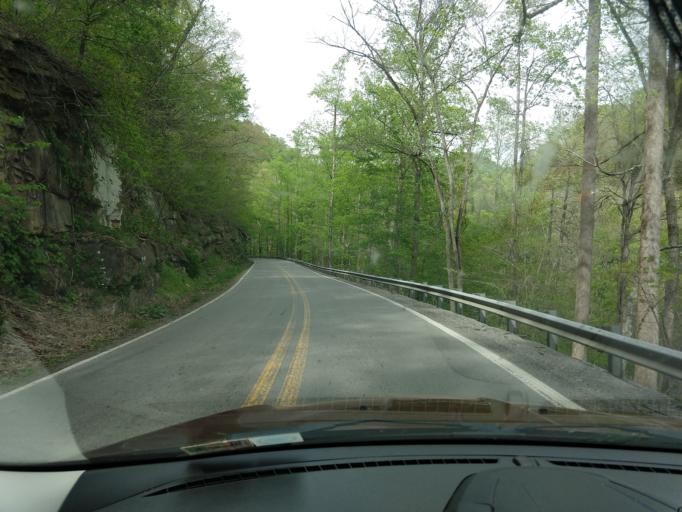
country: US
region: West Virginia
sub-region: McDowell County
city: Welch
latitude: 37.3642
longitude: -81.6420
